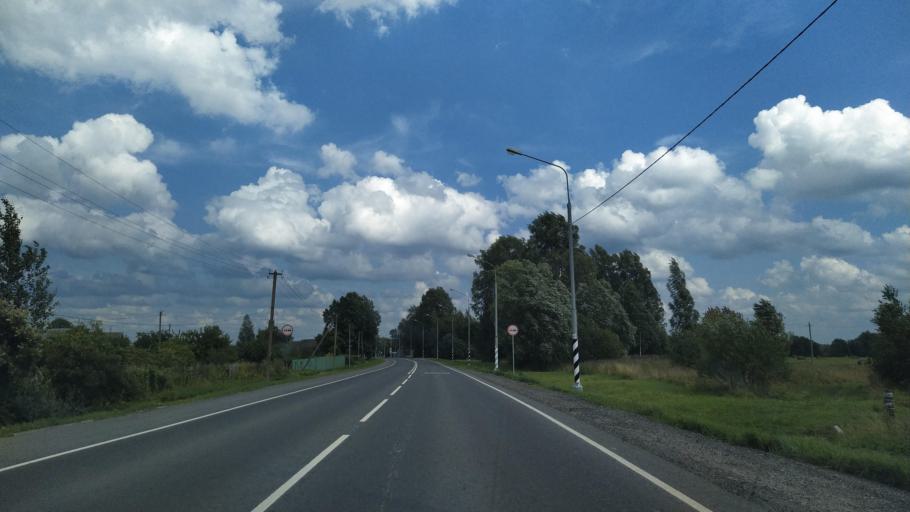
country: RU
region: Pskov
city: Dno
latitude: 58.0614
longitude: 30.0096
